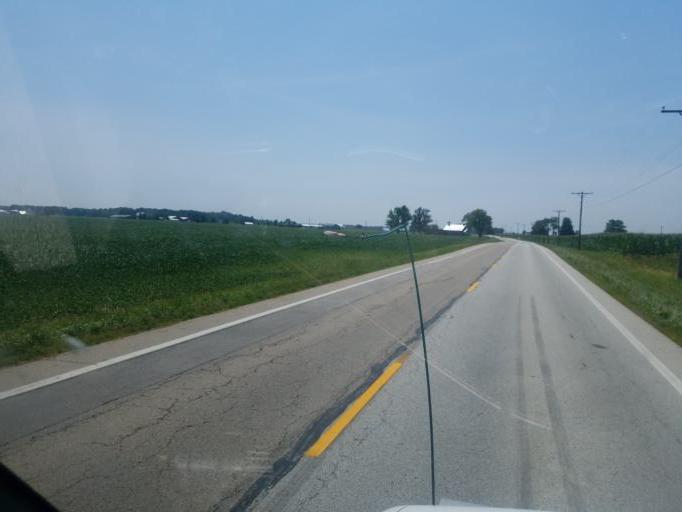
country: US
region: Ohio
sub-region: Shelby County
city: Fort Loramie
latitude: 40.3455
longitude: -84.4116
